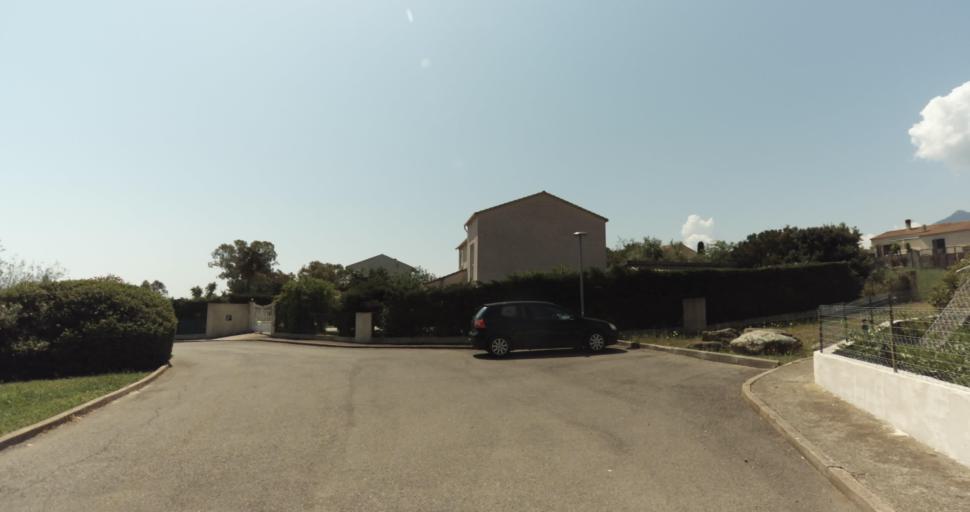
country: FR
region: Corsica
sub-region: Departement de la Haute-Corse
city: Biguglia
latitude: 42.6070
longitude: 9.4329
